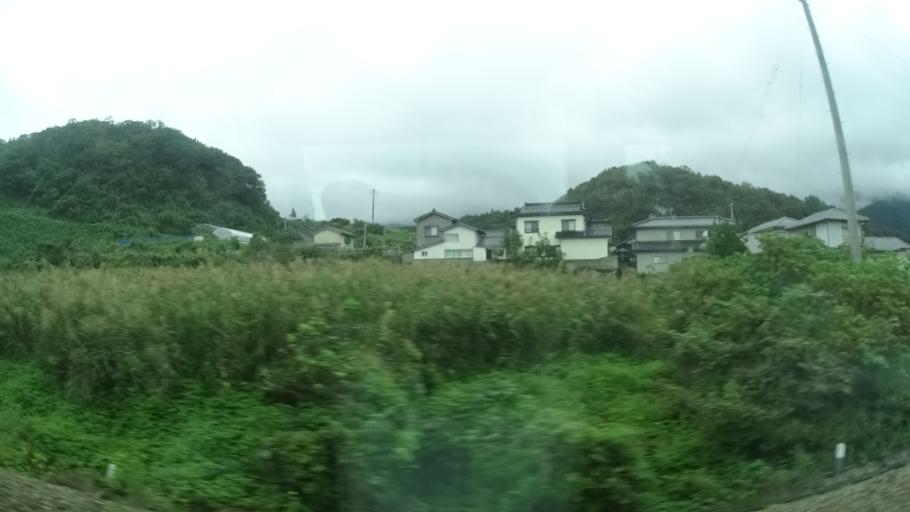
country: JP
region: Yamagata
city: Tsuruoka
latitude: 38.5743
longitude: 139.5585
